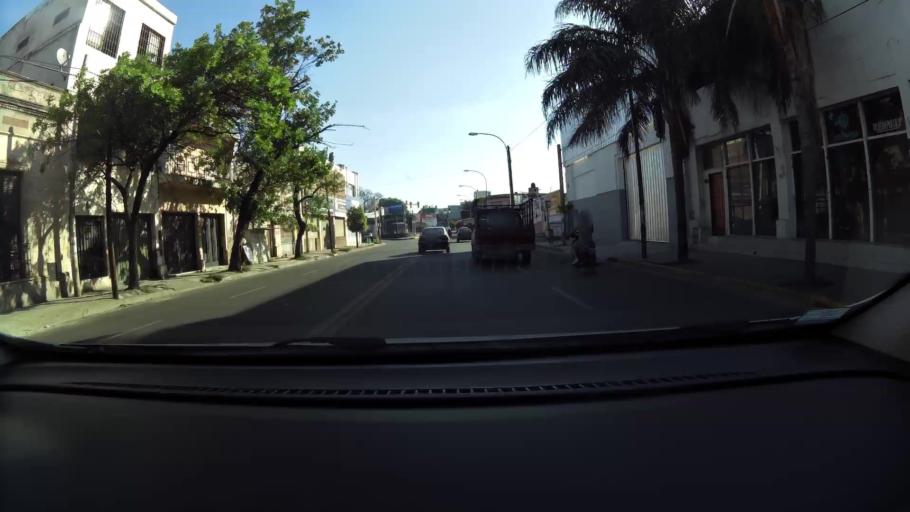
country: AR
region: Cordoba
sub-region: Departamento de Capital
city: Cordoba
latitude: -31.3985
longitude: -64.1707
